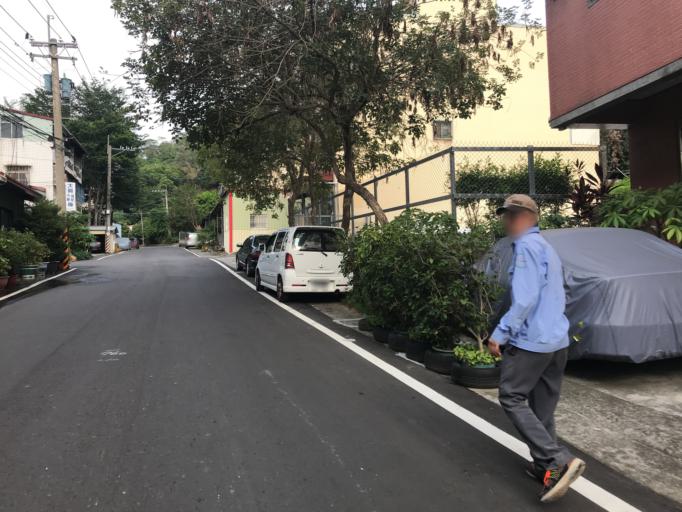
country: TW
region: Taiwan
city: Zhongxing New Village
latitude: 24.0396
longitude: 120.6987
